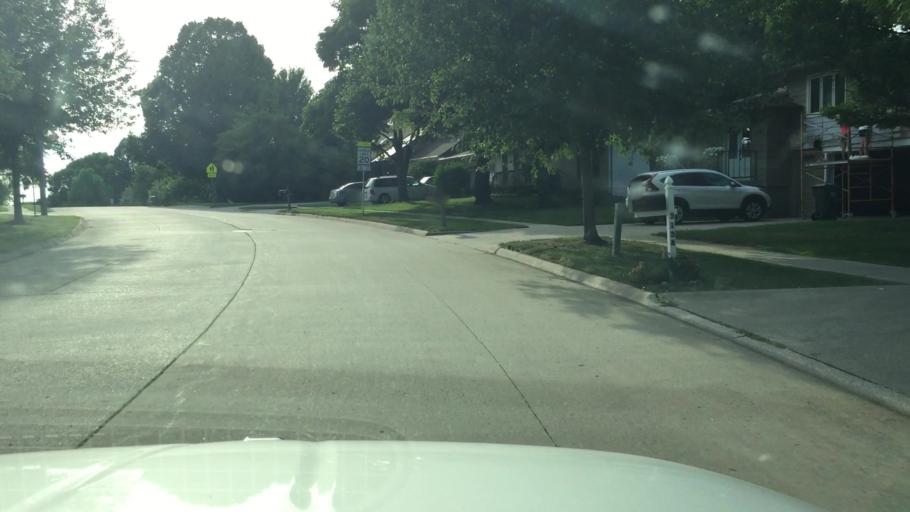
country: US
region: Iowa
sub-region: Johnson County
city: Iowa City
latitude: 41.6610
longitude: -91.4864
